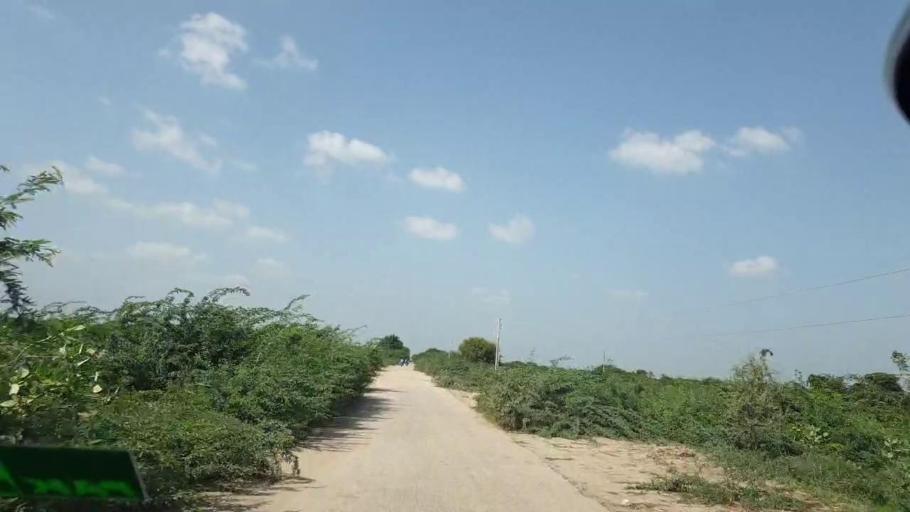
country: PK
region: Sindh
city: Naukot
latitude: 24.6373
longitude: 69.2273
